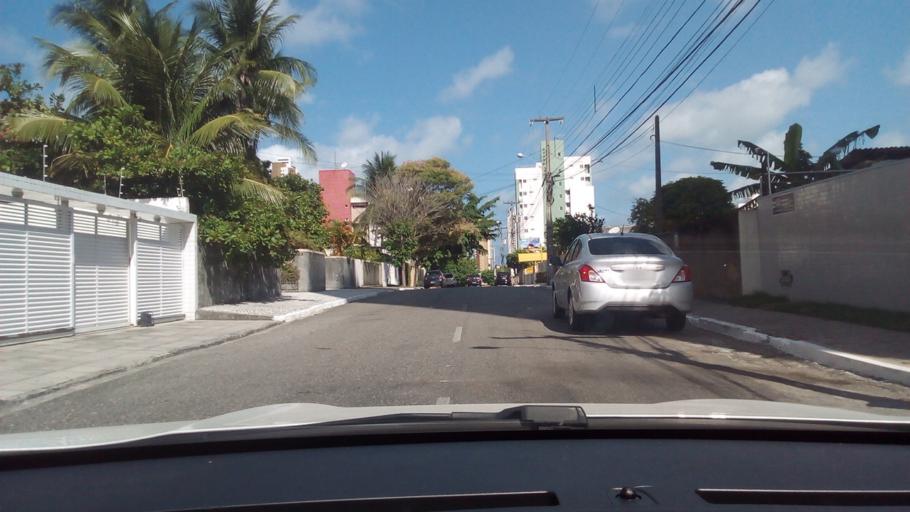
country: BR
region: Paraiba
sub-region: Joao Pessoa
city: Joao Pessoa
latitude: -7.1229
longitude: -34.8410
